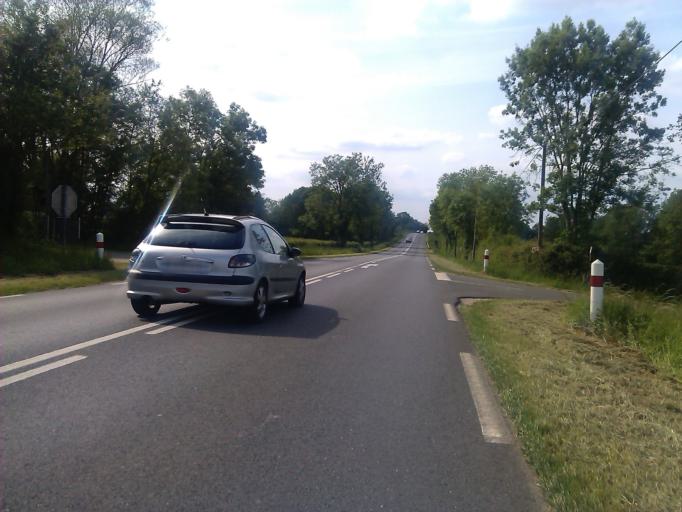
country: FR
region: Centre
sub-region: Departement de l'Indre
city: La Chatre
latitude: 46.5760
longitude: 2.0145
